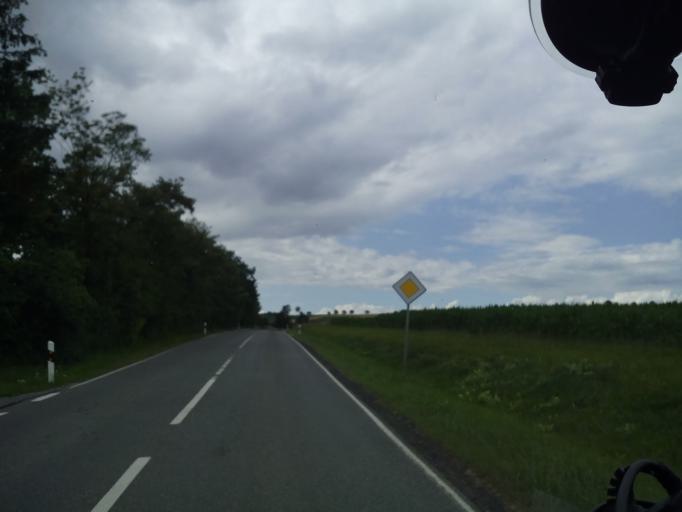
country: DE
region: Bavaria
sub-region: Upper Franconia
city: Sonnefeld
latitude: 50.2409
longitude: 11.1132
